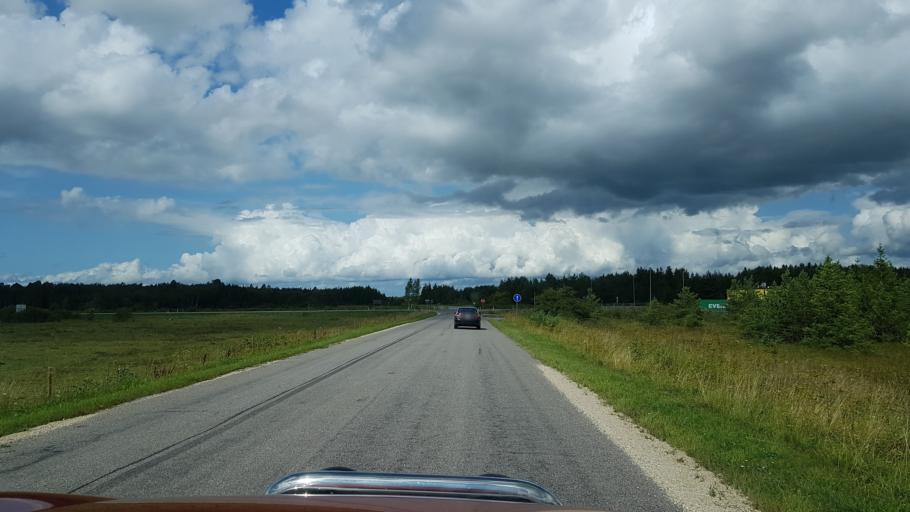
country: EE
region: Laeaene
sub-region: Lihula vald
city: Lihula
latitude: 58.6966
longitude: 23.8291
